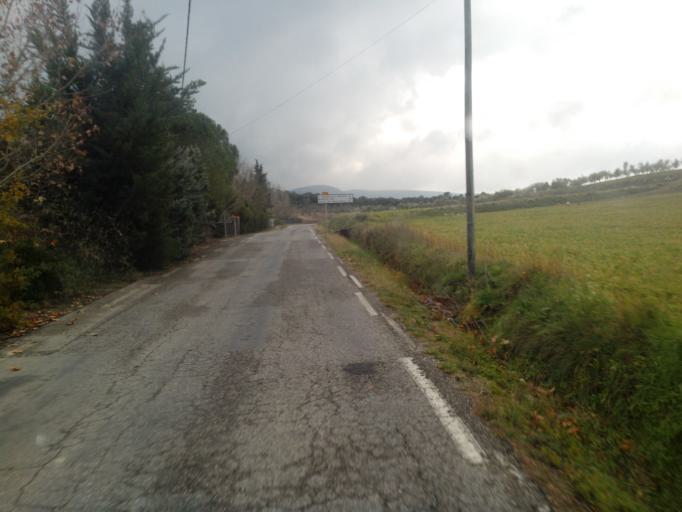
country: FR
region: Languedoc-Roussillon
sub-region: Departement du Gard
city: Saint-Hippolyte-du-Fort
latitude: 43.9538
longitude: 3.8094
